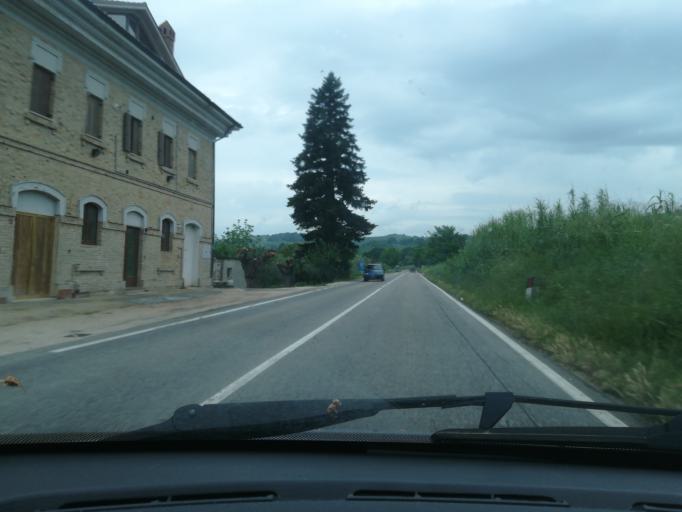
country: IT
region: The Marches
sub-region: Provincia di Macerata
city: Tolentino
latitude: 43.2646
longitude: 13.2495
